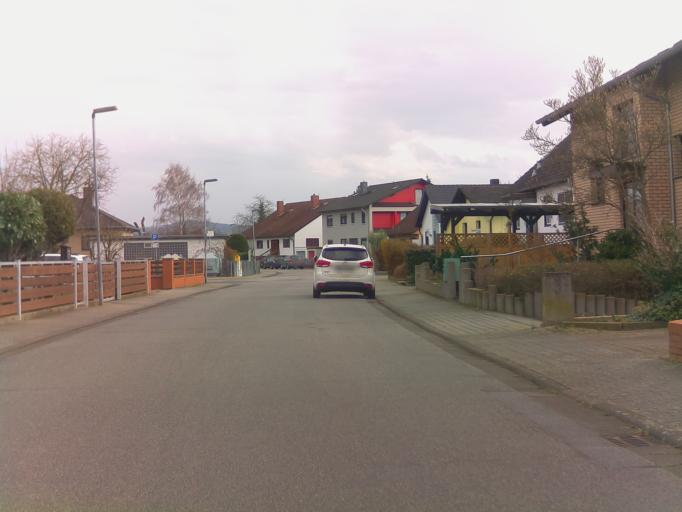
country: DE
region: Hesse
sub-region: Regierungsbezirk Darmstadt
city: Alsbach-Hahnlein
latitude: 49.7334
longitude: 8.5694
